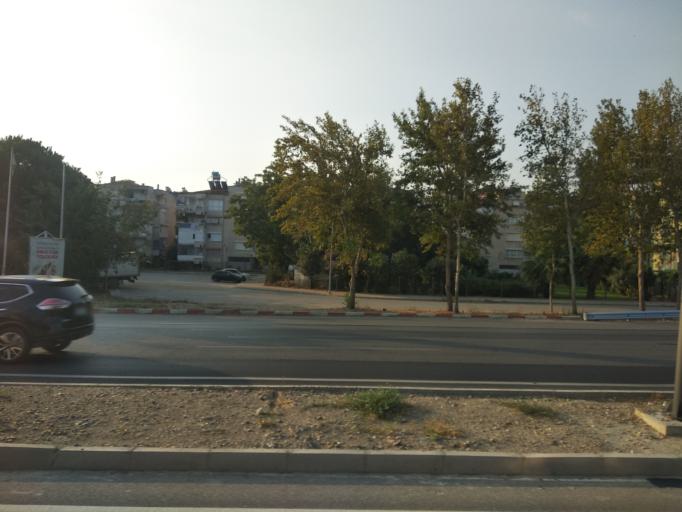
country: TR
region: Manisa
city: Salihli
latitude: 38.4867
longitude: 28.1303
